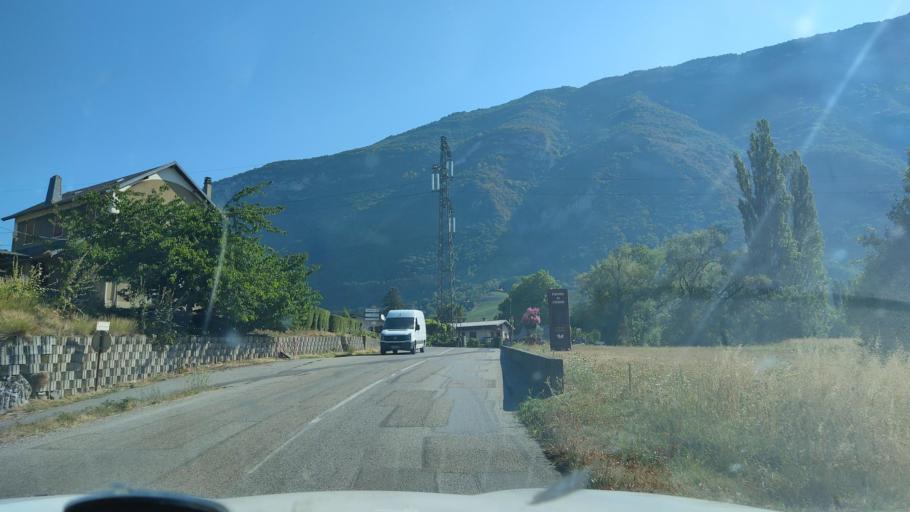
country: FR
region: Rhone-Alpes
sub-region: Departement de la Savoie
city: Les Marches
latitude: 45.5207
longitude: 6.0066
